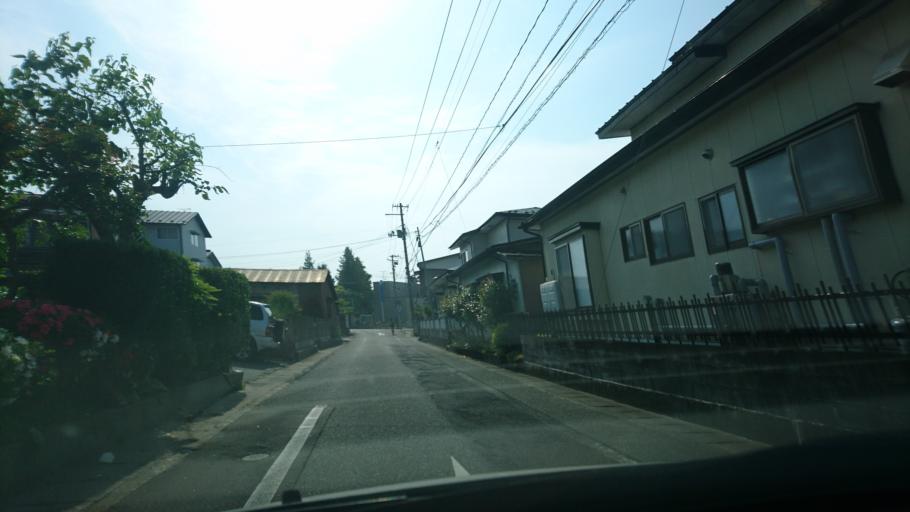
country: JP
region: Iwate
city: Ichinoseki
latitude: 38.9299
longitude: 141.1415
